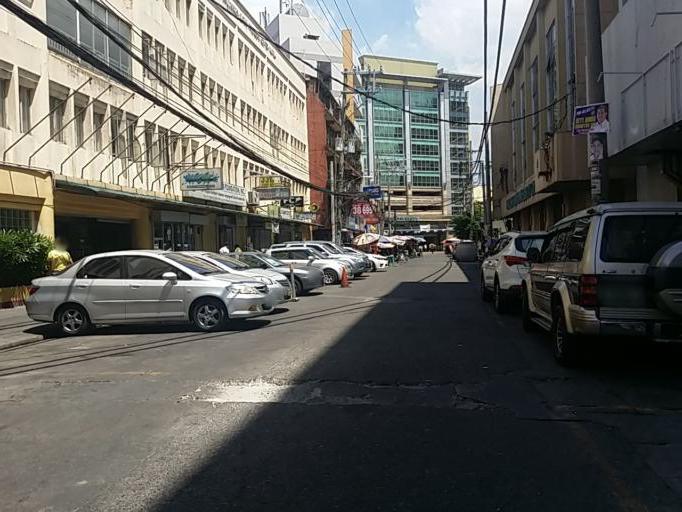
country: PH
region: Metro Manila
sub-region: City of Manila
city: Quiapo
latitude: 14.6035
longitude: 120.9885
